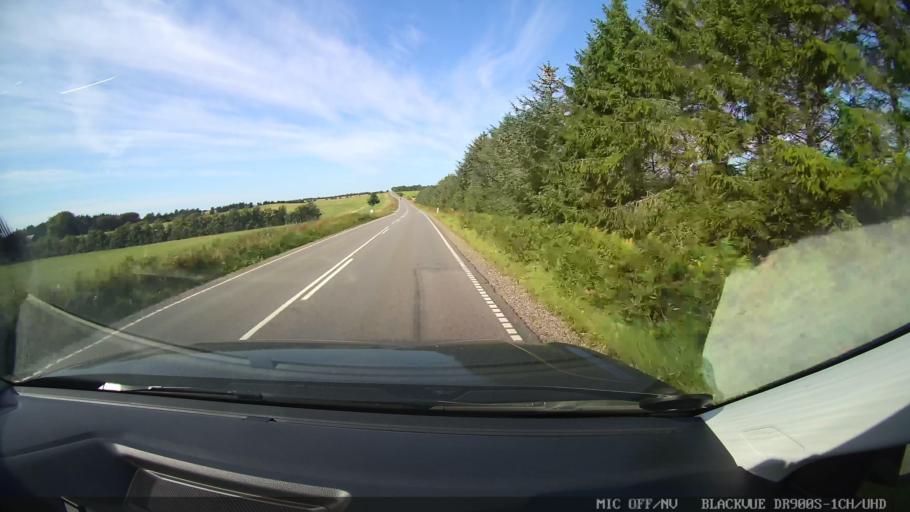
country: DK
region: North Denmark
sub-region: Mariagerfjord Kommune
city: Mariager
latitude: 56.6894
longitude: 9.9420
